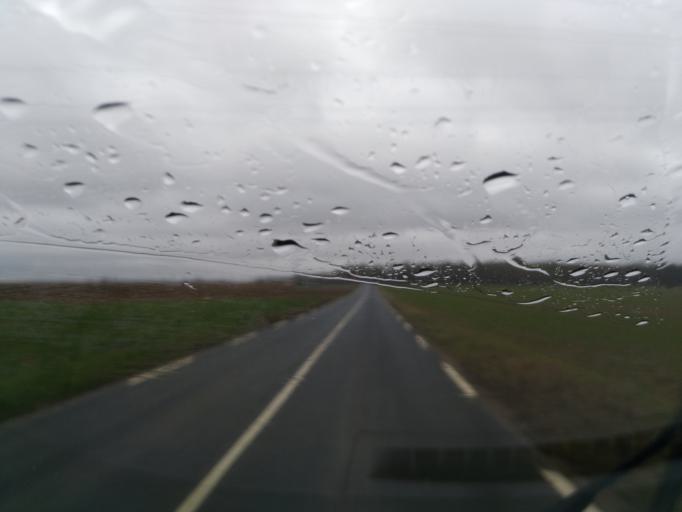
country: FR
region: Ile-de-France
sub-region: Departement des Yvelines
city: Thoiry
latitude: 48.8573
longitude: 1.8317
